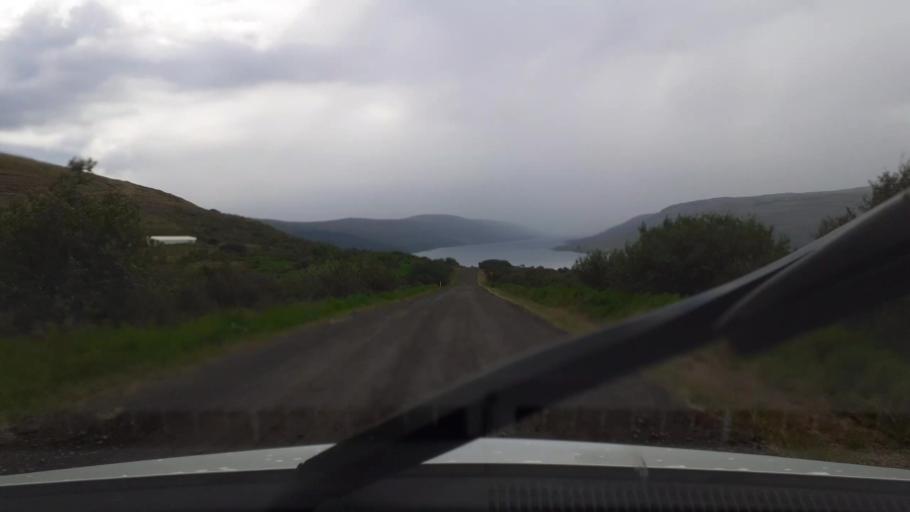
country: IS
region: Capital Region
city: Mosfellsbaer
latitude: 64.5263
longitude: -21.4845
